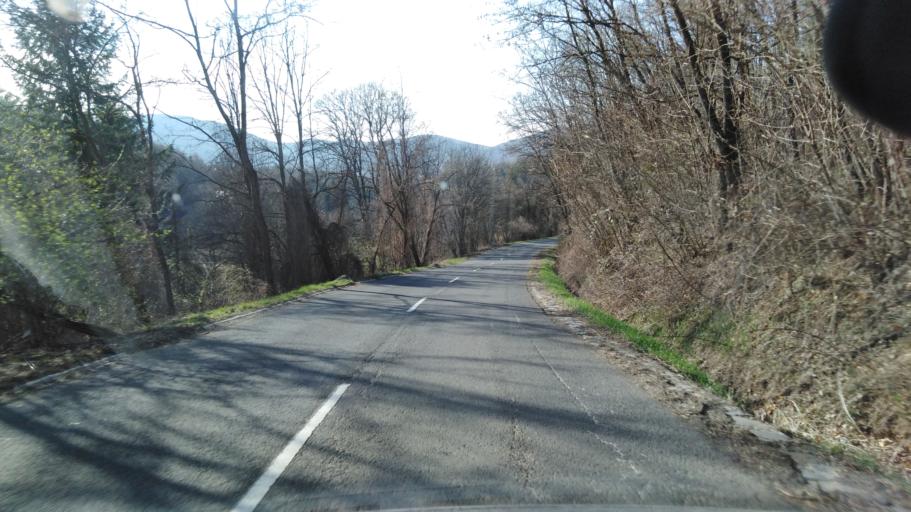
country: HU
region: Nograd
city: Somoskoujfalu
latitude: 48.1594
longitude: 19.8478
